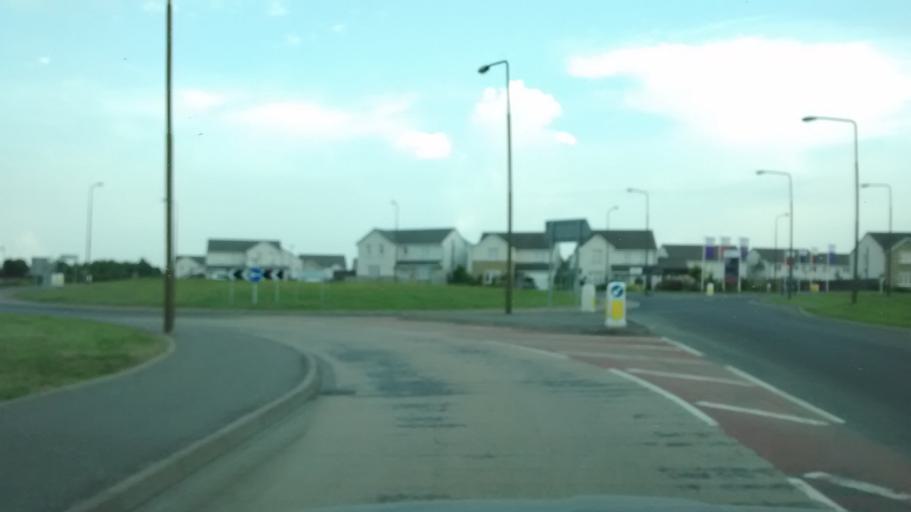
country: GB
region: Scotland
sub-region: West Lothian
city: Armadale
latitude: 55.8871
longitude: -3.6984
